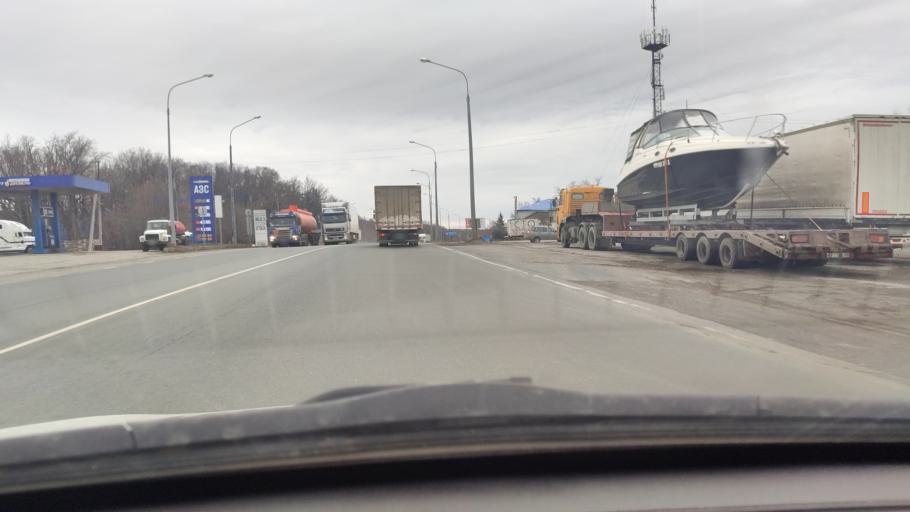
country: RU
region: Samara
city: Zhigulevsk
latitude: 53.3839
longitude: 49.4558
